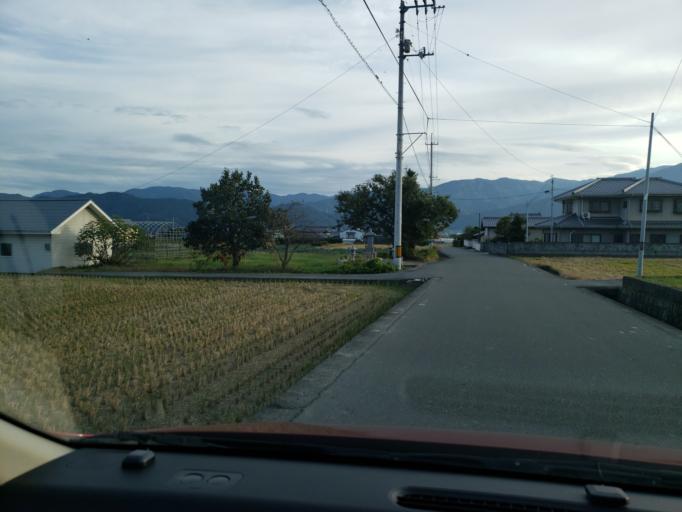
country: JP
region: Tokushima
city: Wakimachi
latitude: 34.0861
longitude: 134.2267
